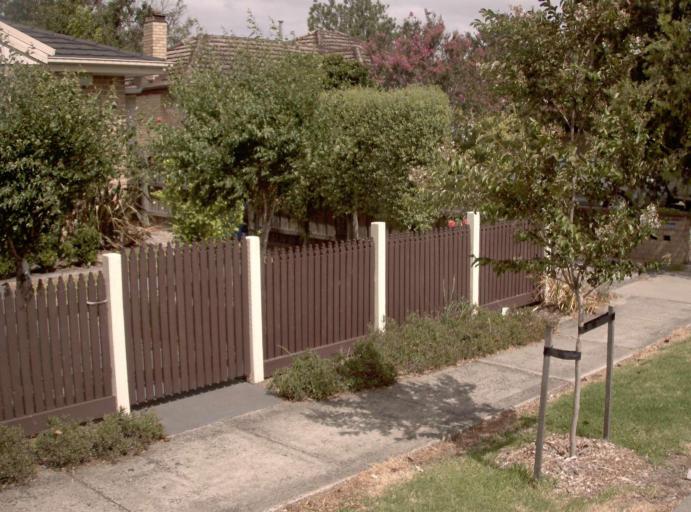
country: AU
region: Victoria
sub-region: Greater Dandenong
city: Springvale
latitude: -37.9342
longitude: 145.1595
